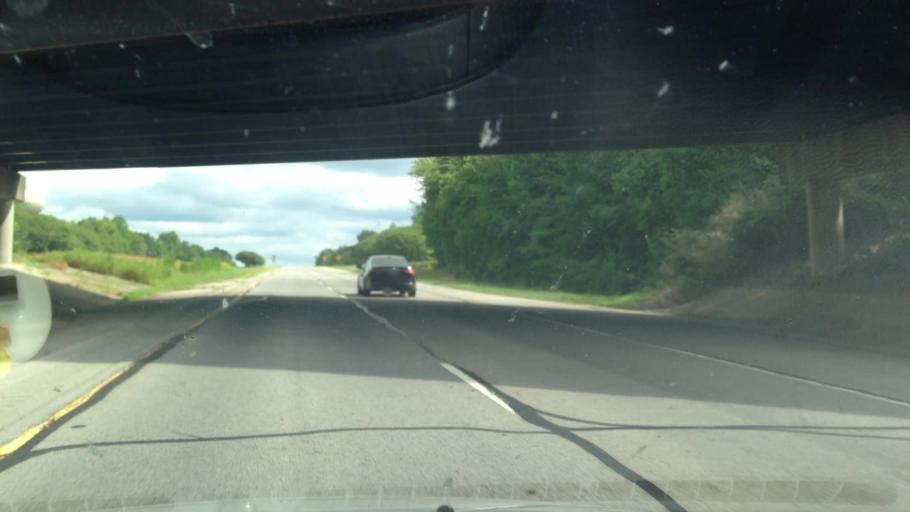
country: US
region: Virginia
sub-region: City of Danville
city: Danville
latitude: 36.5189
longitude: -79.4744
